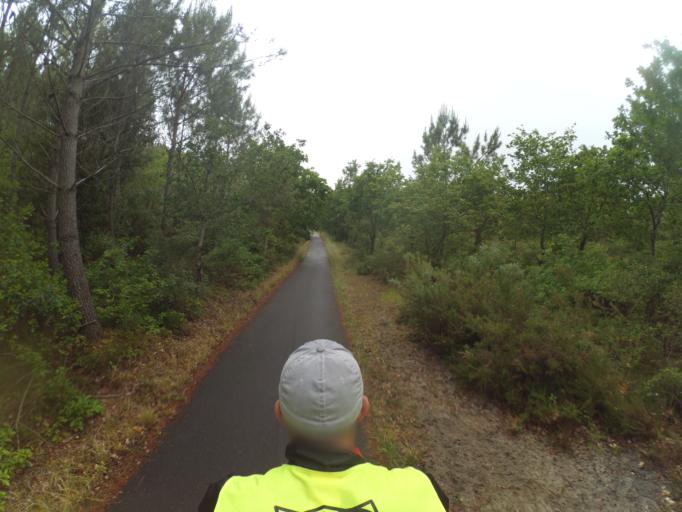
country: FR
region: Aquitaine
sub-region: Departement des Landes
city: Mimizan
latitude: 44.2190
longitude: -1.2391
